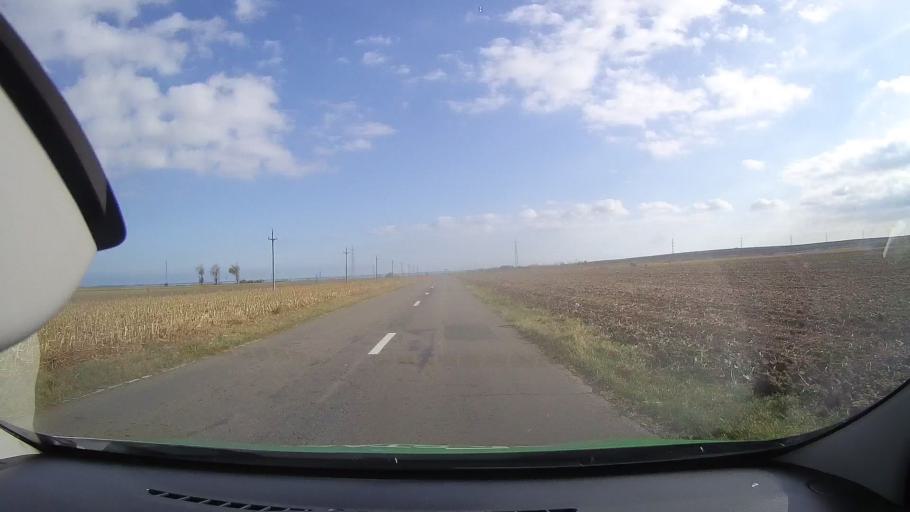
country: RO
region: Constanta
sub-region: Comuna Istria
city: Nuntasi
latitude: 44.5307
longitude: 28.6773
